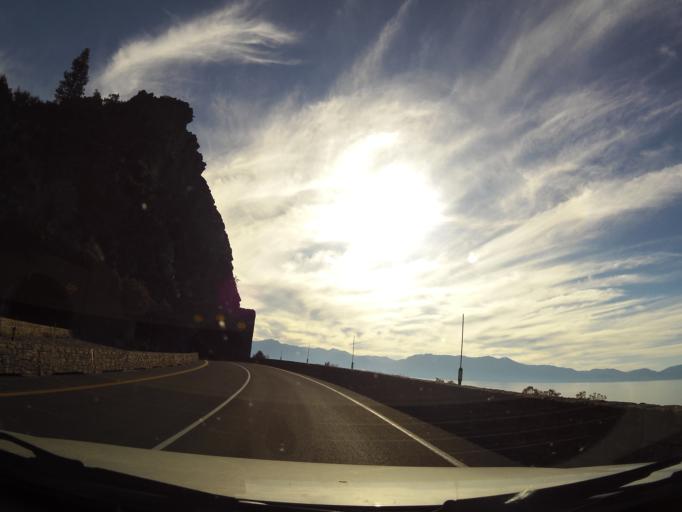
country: US
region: Nevada
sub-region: Douglas County
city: Kingsbury
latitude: 39.0475
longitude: -119.9479
